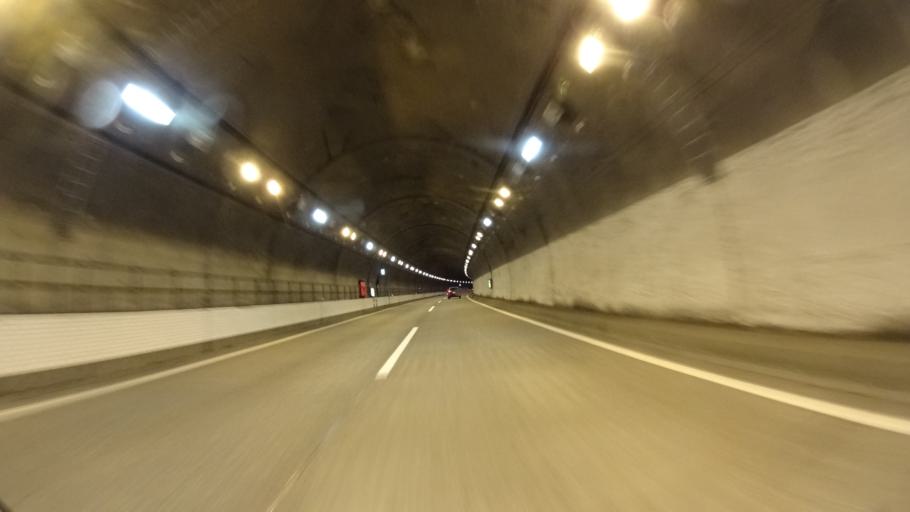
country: JP
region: Nagano
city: Nagano-shi
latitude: 36.5604
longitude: 138.1680
